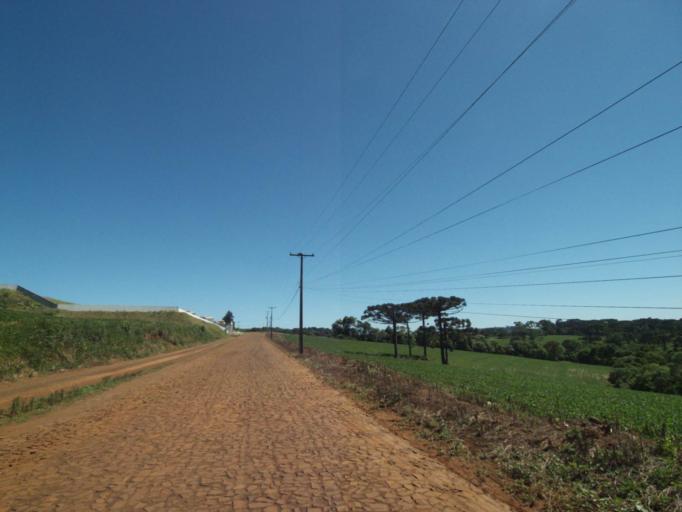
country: BR
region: Parana
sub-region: Pato Branco
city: Pato Branco
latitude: -26.2588
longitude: -52.7823
